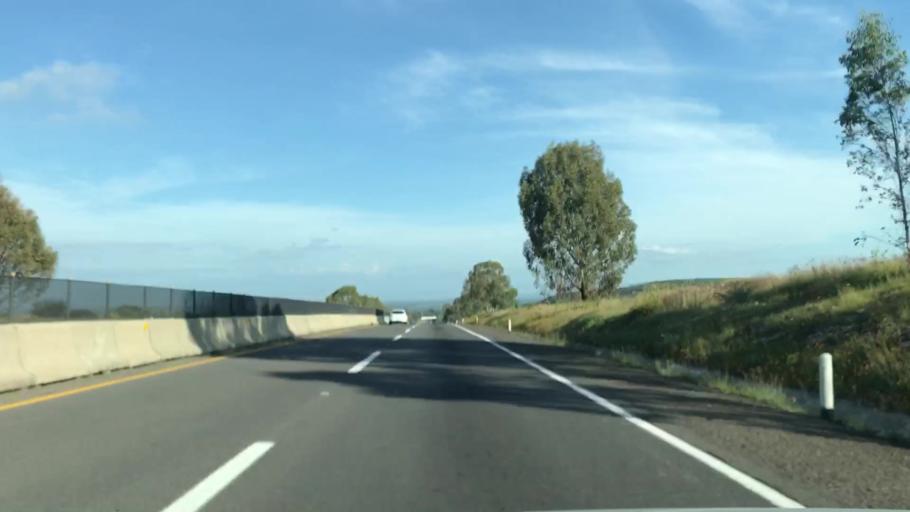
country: MX
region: Jalisco
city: Encarnacion de Diaz
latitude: 21.3862
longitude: -102.1421
